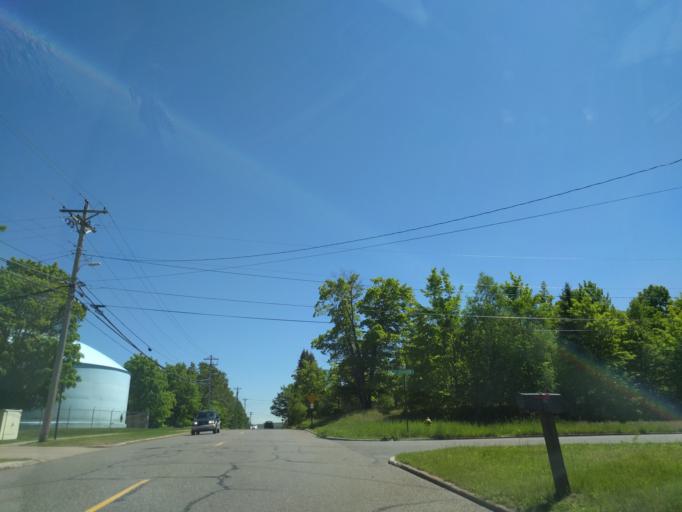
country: US
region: Michigan
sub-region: Marquette County
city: Marquette
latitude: 46.5503
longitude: -87.4123
